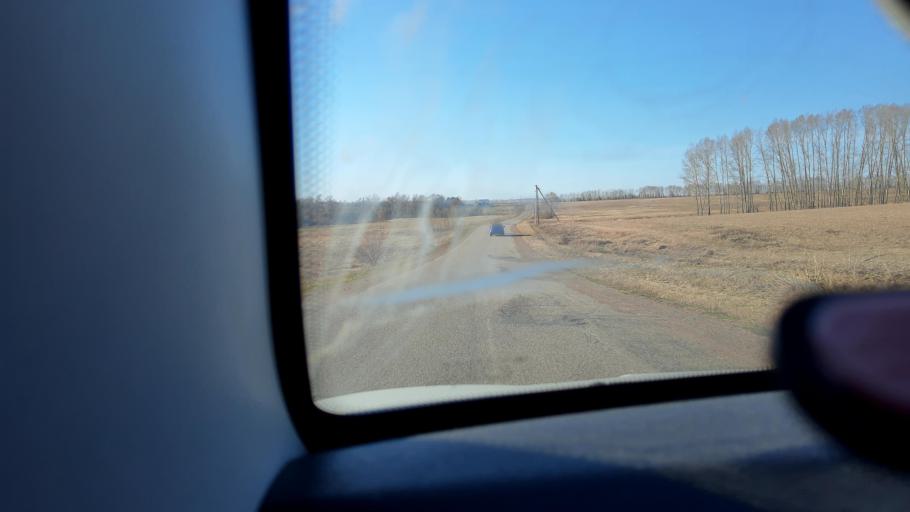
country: RU
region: Bashkortostan
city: Asanovo
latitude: 54.8268
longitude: 55.4659
